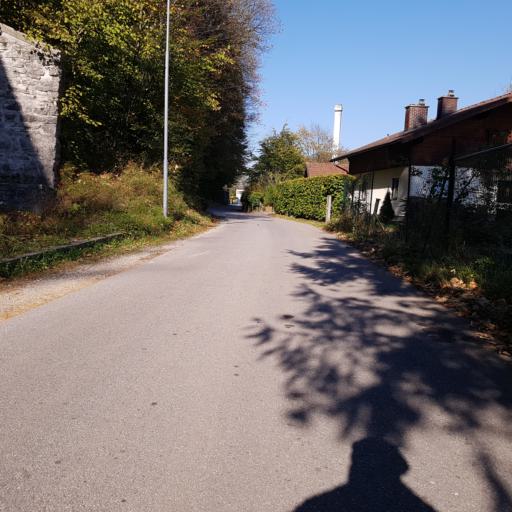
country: AT
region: Salzburg
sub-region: Politischer Bezirk Hallein
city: Hallein
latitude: 47.6685
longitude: 13.1078
